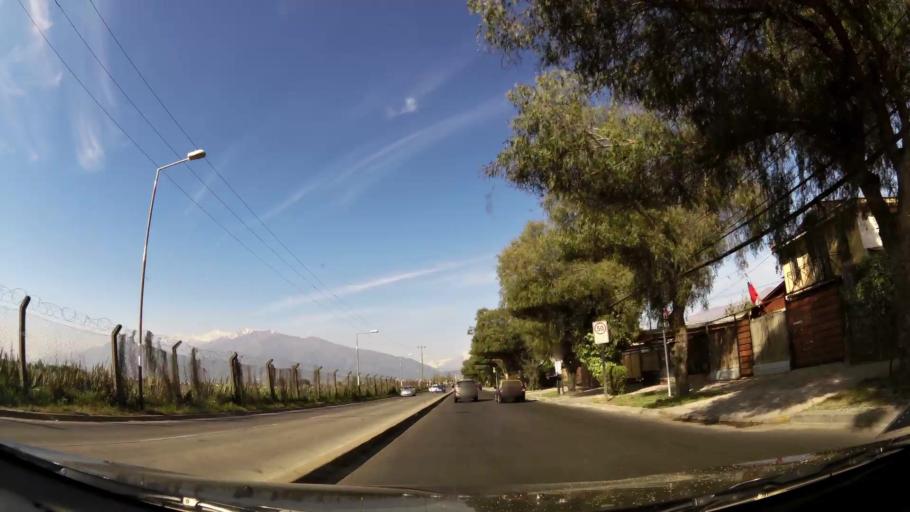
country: CL
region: Santiago Metropolitan
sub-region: Provincia de Cordillera
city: Puente Alto
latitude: -33.6060
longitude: -70.6007
